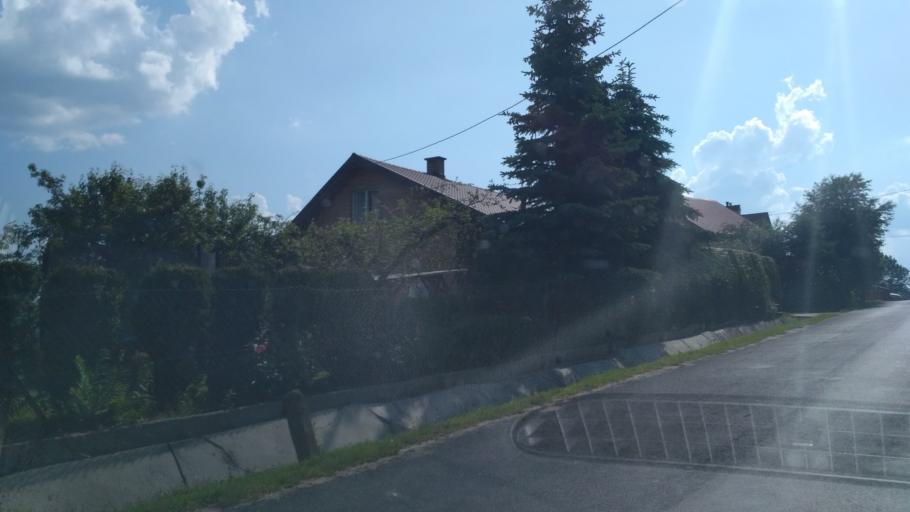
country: PL
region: Subcarpathian Voivodeship
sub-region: Powiat jaroslawski
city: Rokietnica
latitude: 49.9257
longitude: 22.6985
